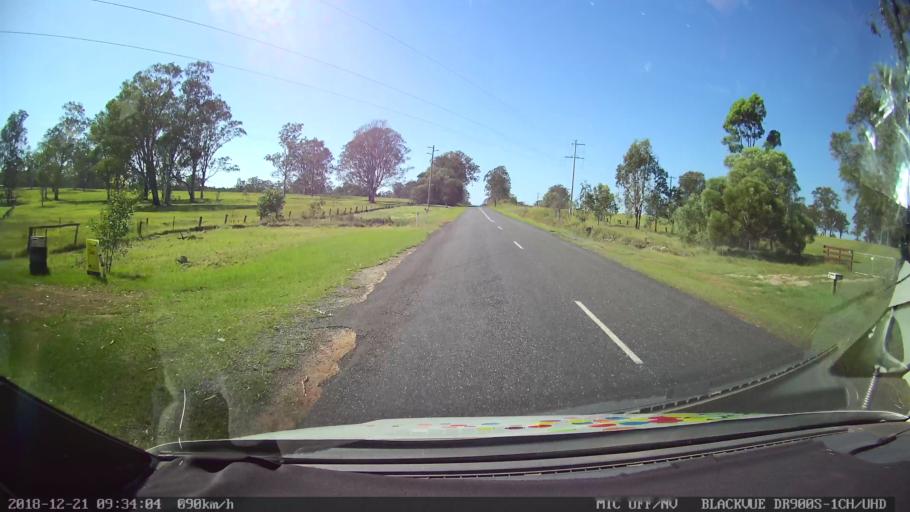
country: AU
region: New South Wales
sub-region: Clarence Valley
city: Grafton
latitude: -29.4932
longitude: 152.9785
